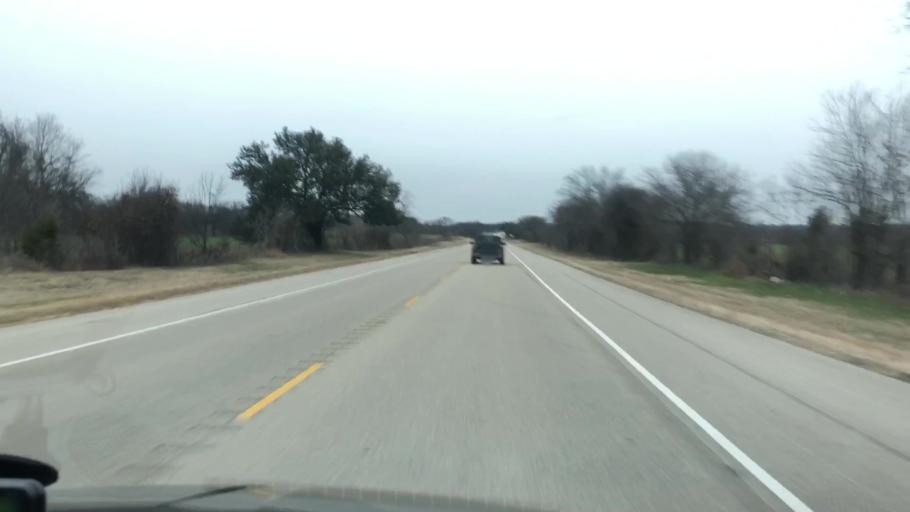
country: US
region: Texas
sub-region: Hamilton County
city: Hamilton
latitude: 31.6026
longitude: -98.1579
